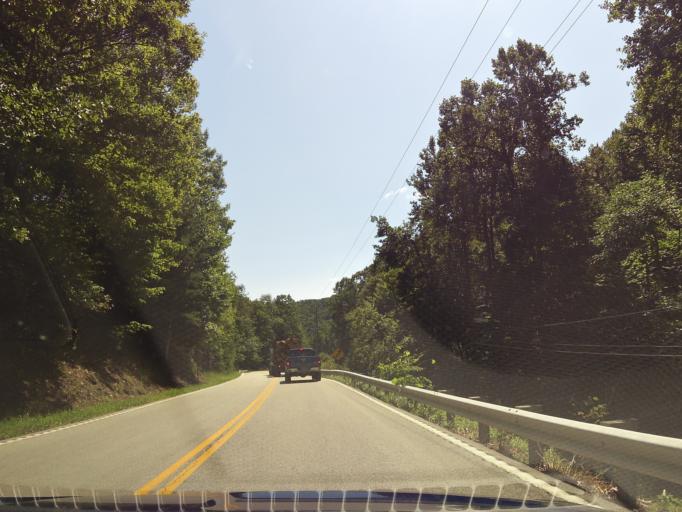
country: US
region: Kentucky
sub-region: Leslie County
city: Hyden
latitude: 37.1333
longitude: -83.4656
